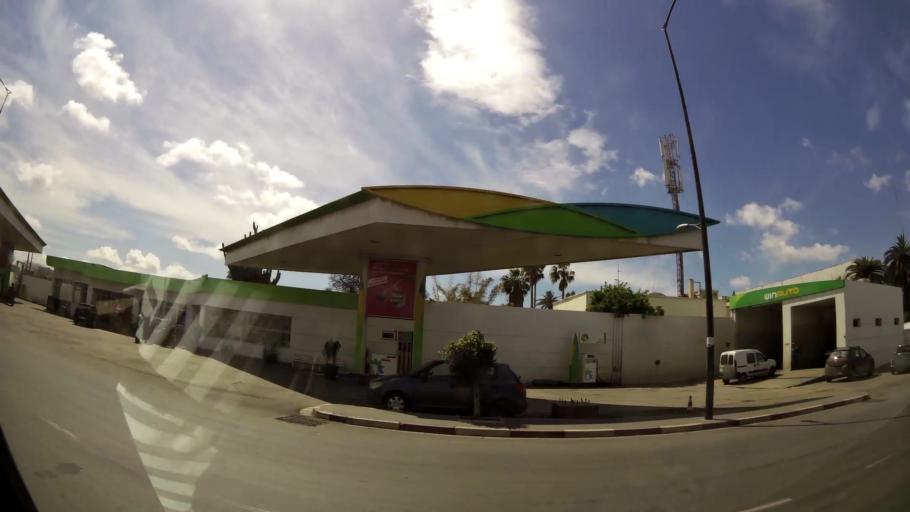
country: MA
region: Grand Casablanca
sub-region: Casablanca
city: Casablanca
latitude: 33.6040
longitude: -7.5460
